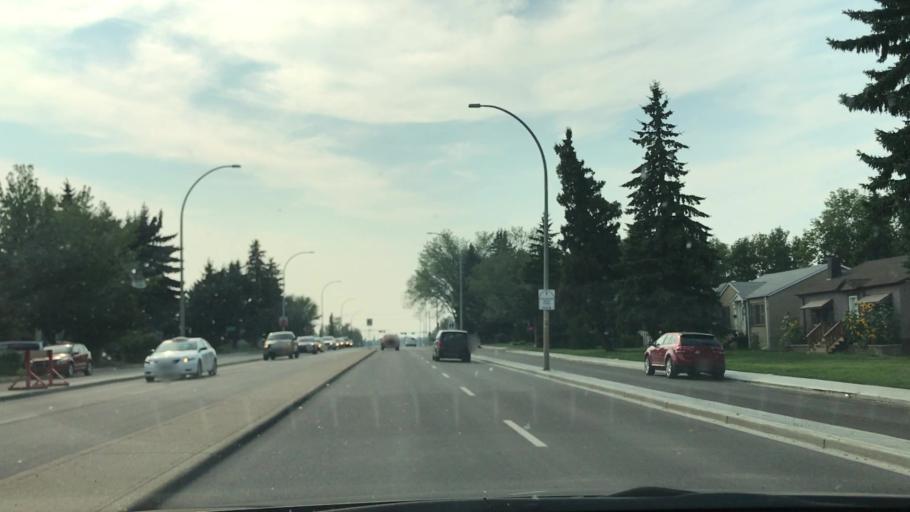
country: CA
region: Alberta
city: Edmonton
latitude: 53.4982
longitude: -113.5079
